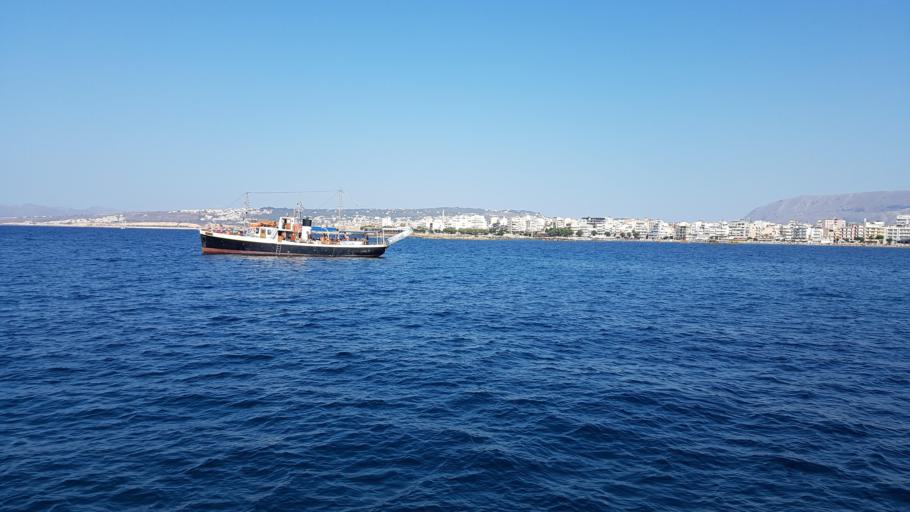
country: GR
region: Crete
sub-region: Nomos Chanias
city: Chania
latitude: 35.5176
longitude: 23.9994
